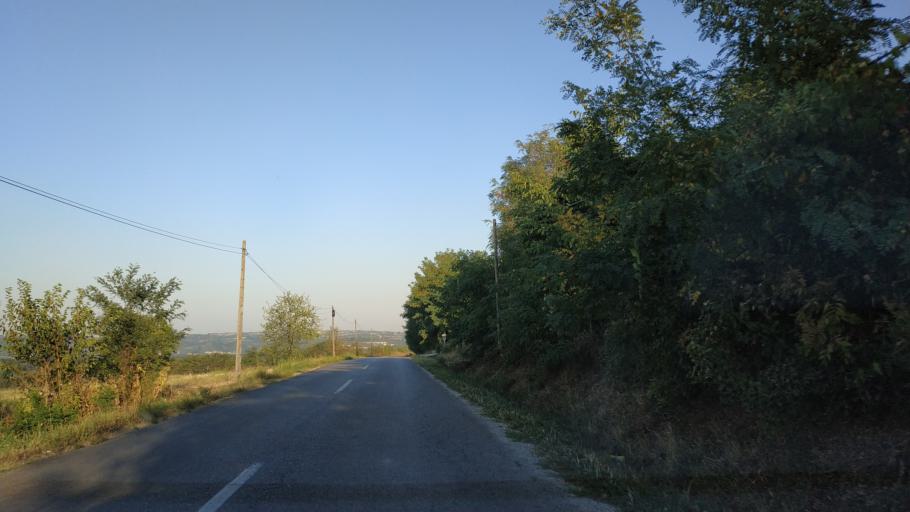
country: RS
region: Central Serbia
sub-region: Sumadijski Okrug
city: Topola
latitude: 44.2714
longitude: 20.6467
